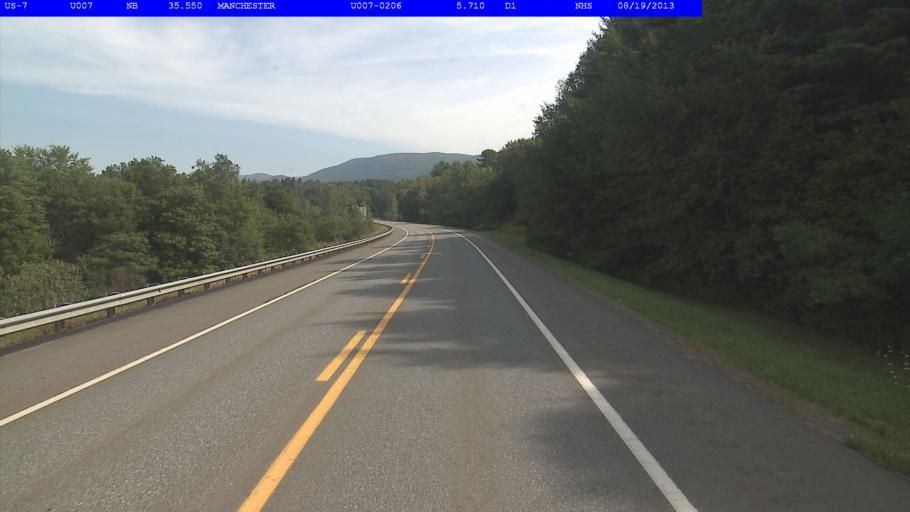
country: US
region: Vermont
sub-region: Bennington County
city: Manchester Center
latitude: 43.1852
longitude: -73.0174
